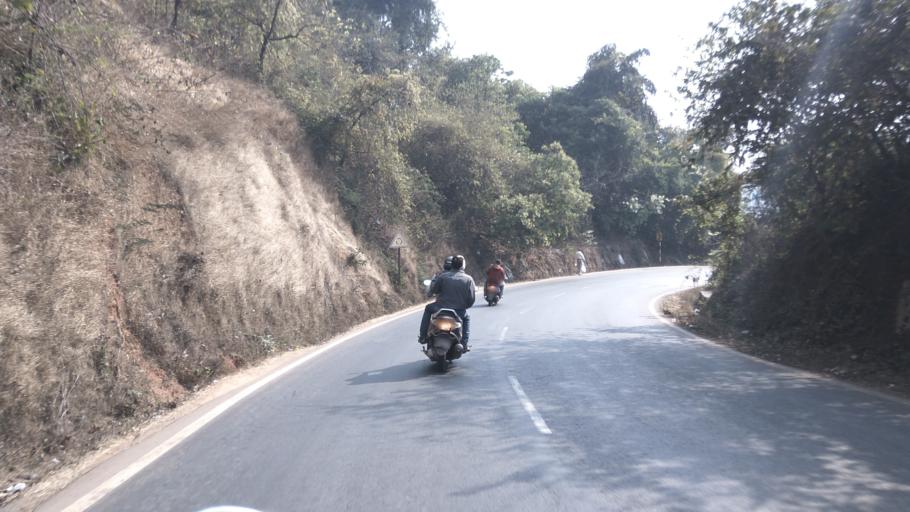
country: IN
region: Goa
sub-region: North Goa
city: Bandora
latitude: 15.4560
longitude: 73.9662
